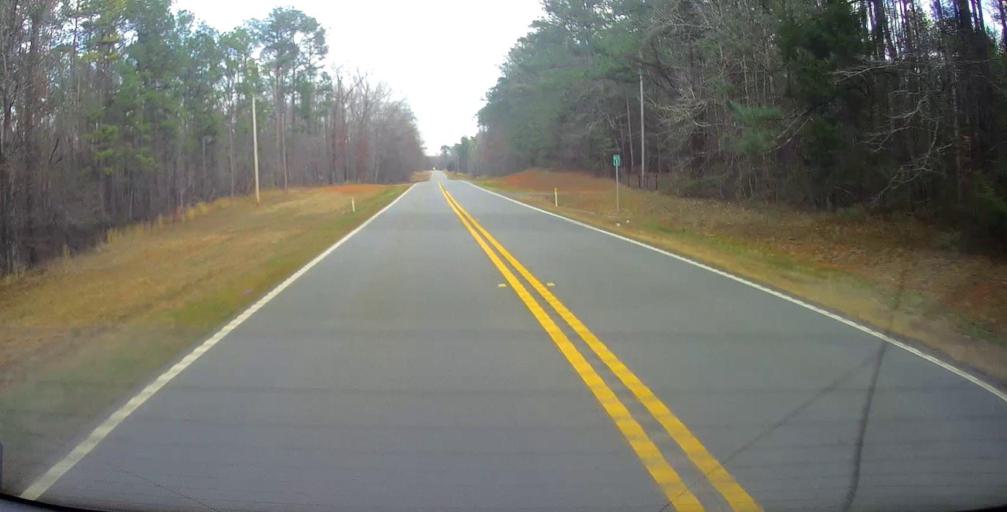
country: US
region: Georgia
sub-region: Harris County
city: Hamilton
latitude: 32.7018
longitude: -84.8420
